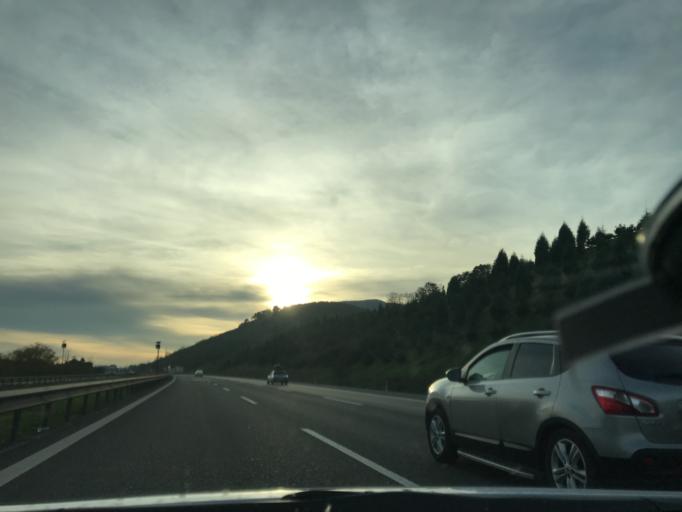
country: TR
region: Duzce
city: Gumusova
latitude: 40.8274
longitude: 30.9249
